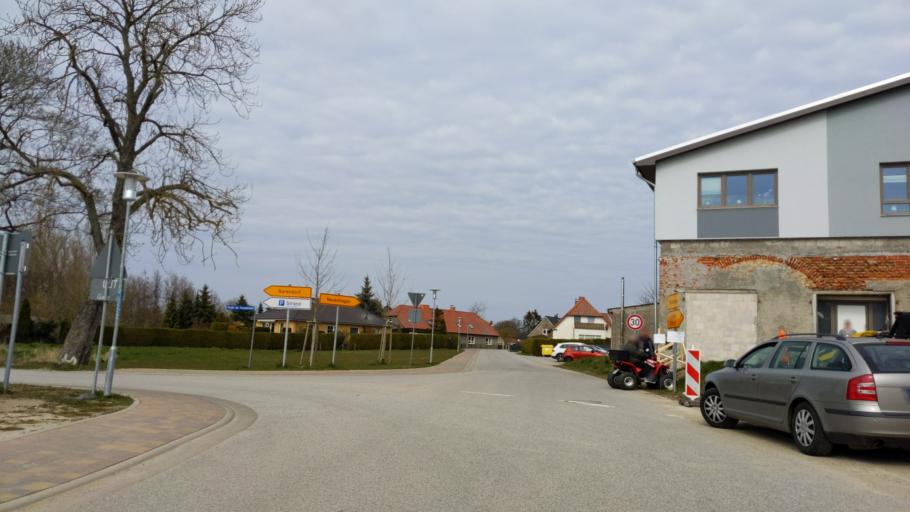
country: DE
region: Mecklenburg-Vorpommern
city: Dassow
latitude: 53.9574
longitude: 10.9756
